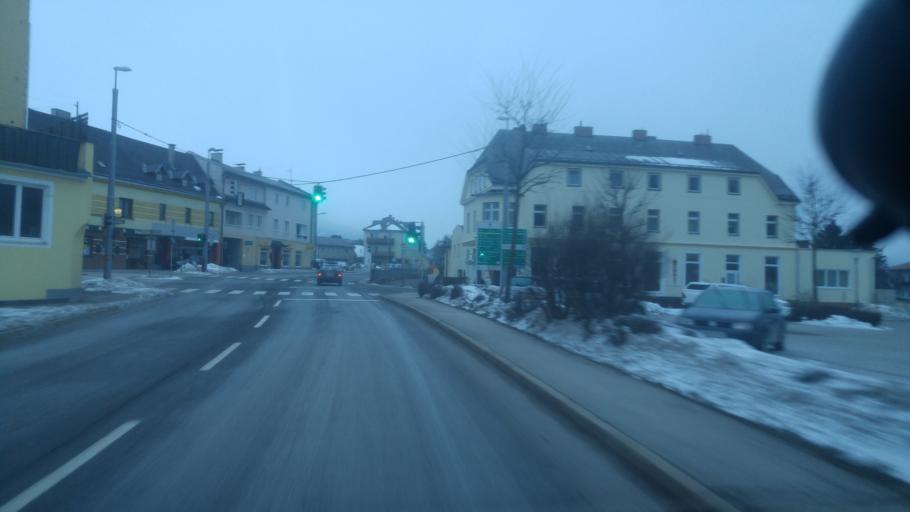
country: AT
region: Lower Austria
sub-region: Politischer Bezirk Lilienfeld
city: Hainfeld
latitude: 48.0364
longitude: 15.7716
